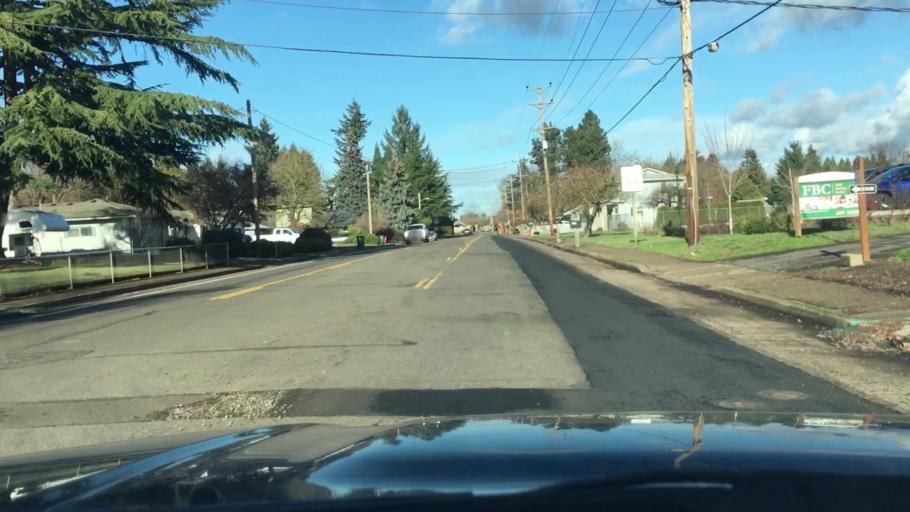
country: US
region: Oregon
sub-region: Lane County
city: Eugene
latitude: 44.0669
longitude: -123.1630
